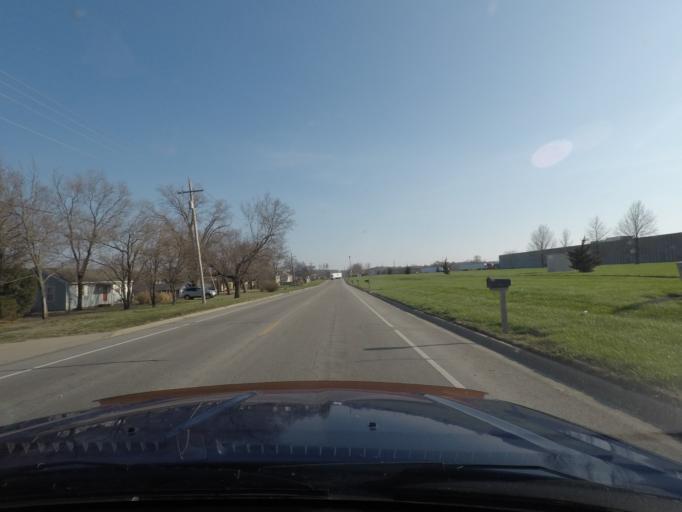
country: US
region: Kansas
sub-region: Douglas County
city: Lawrence
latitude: 38.9962
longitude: -95.2605
